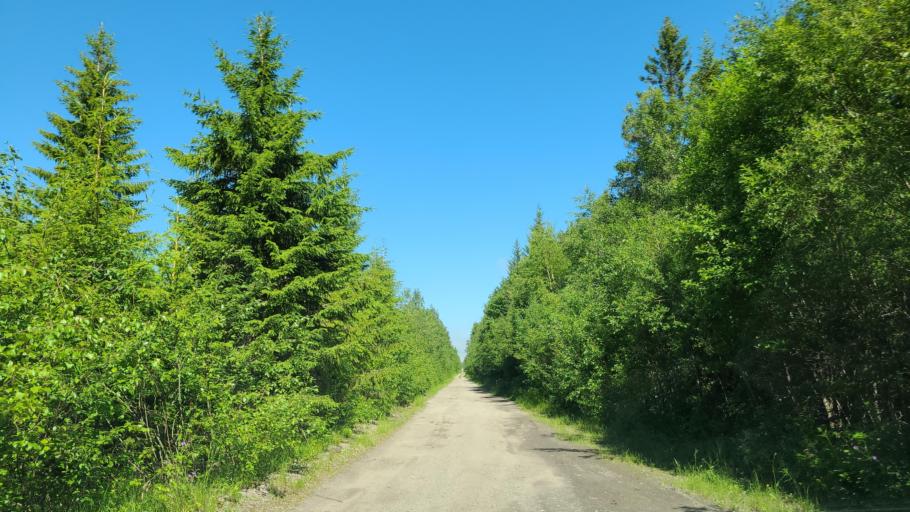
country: SE
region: Vaesternorrland
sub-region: OErnskoeldsviks Kommun
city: Husum
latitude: 63.4222
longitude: 19.2240
